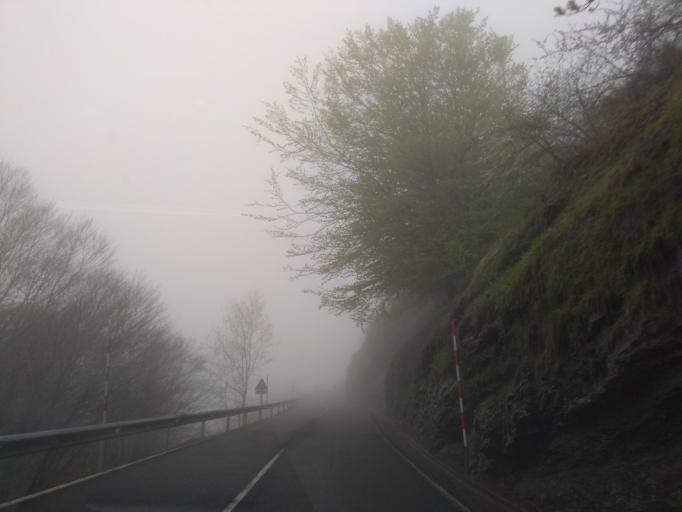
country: ES
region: Basque Country
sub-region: Bizkaia
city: Lanestosa
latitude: 43.1530
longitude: -3.4411
